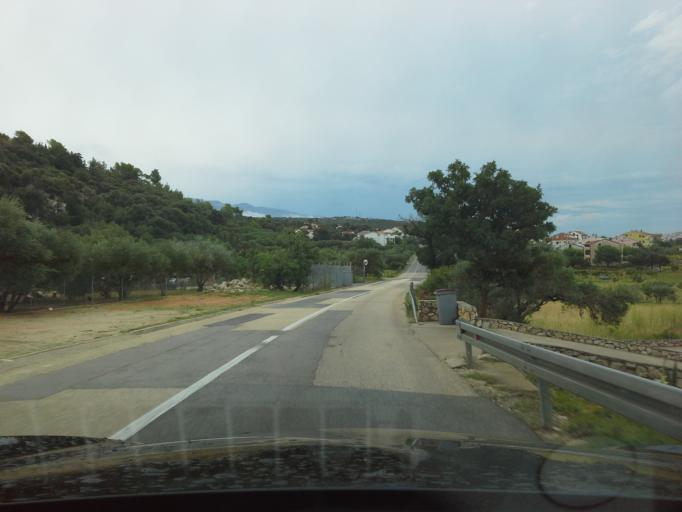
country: HR
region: Primorsko-Goranska
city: Banjol
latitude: 44.7344
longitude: 14.8079
